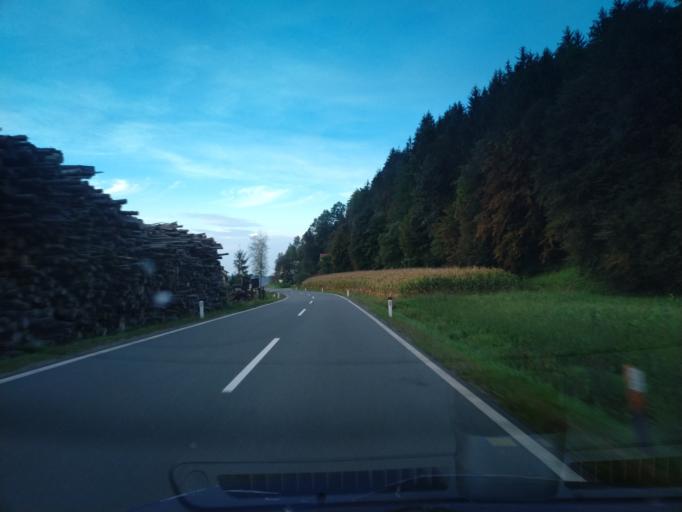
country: AT
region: Styria
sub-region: Politischer Bezirk Leibnitz
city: Sankt Johann im Saggautal
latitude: 46.6901
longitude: 15.3955
